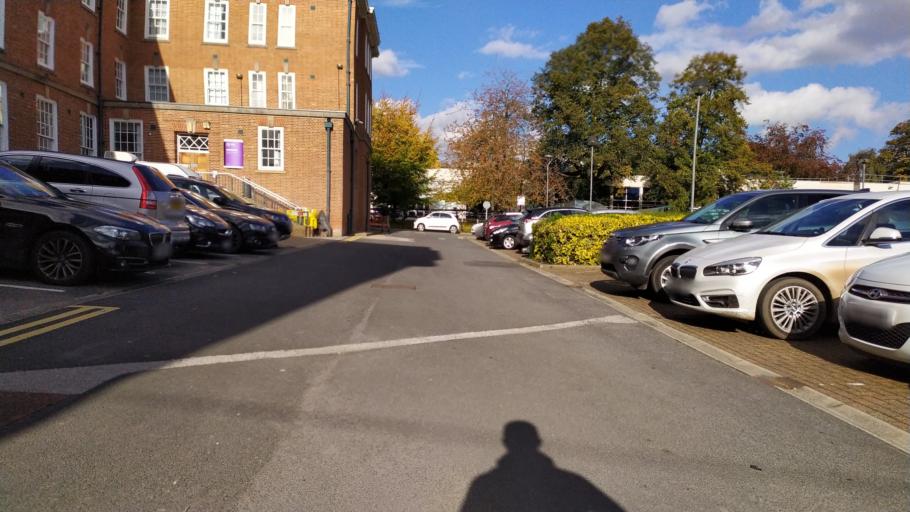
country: GB
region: England
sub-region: City and Borough of Leeds
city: Horsforth
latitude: 53.8268
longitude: -1.5915
